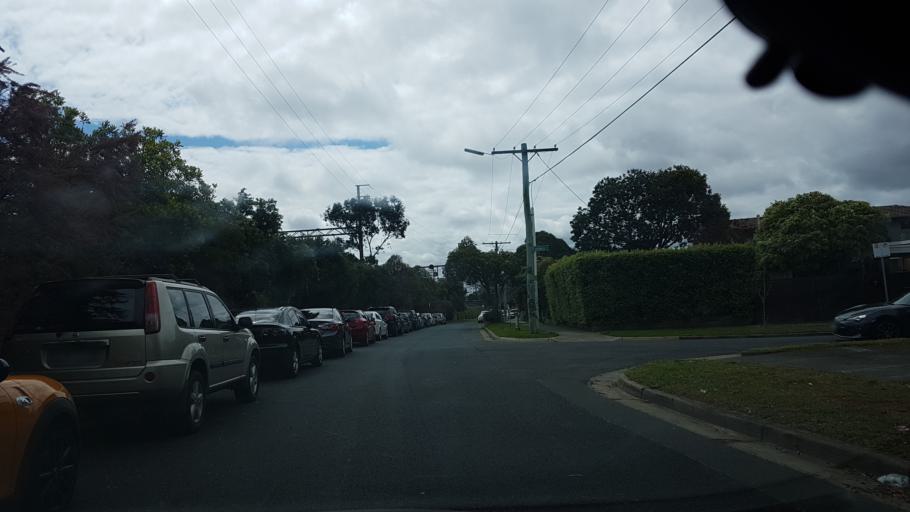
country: AU
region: Victoria
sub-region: Glen Eira
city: Bentleigh
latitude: -37.9274
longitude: 145.0358
